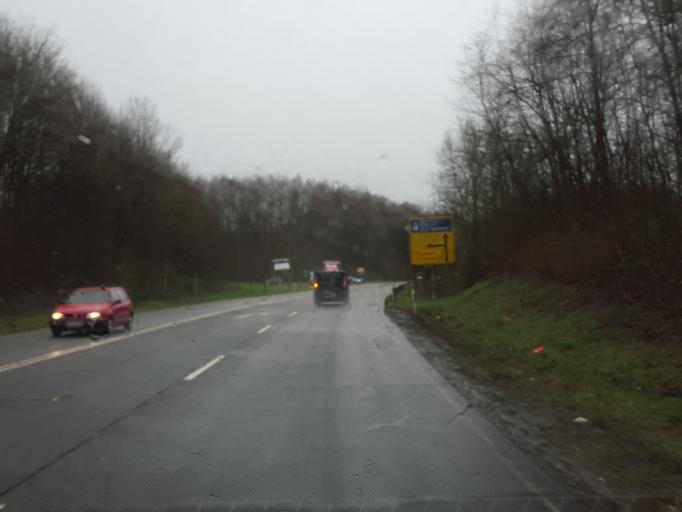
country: DE
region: Saarland
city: Neunkirchen
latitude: 49.3386
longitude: 7.1732
